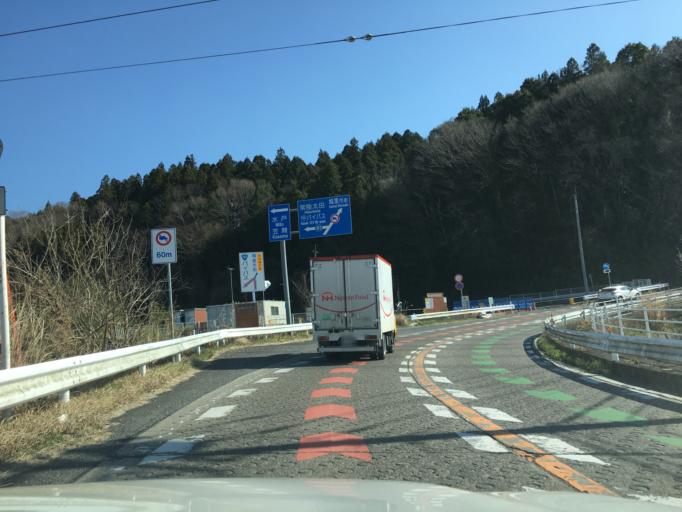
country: JP
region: Ibaraki
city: Omiya
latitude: 36.4881
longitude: 140.3770
